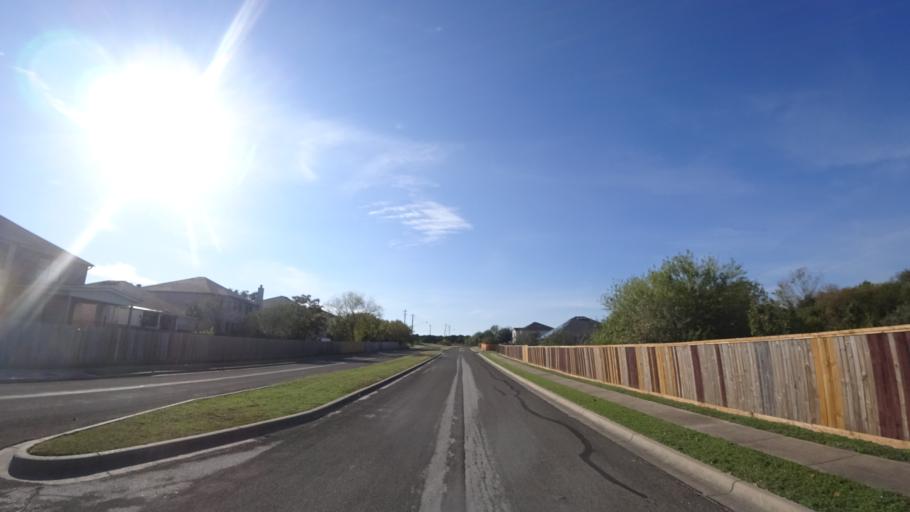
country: US
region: Texas
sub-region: Travis County
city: Pflugerville
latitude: 30.4032
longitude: -97.6516
